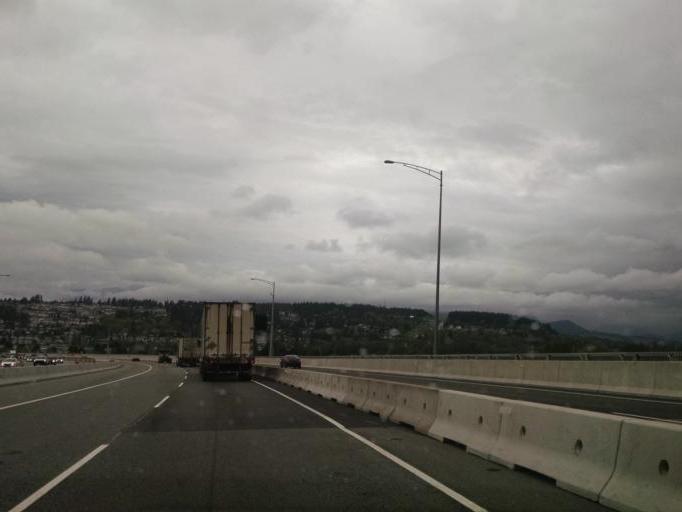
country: CA
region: British Columbia
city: Port Moody
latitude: 49.2228
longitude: -122.8144
